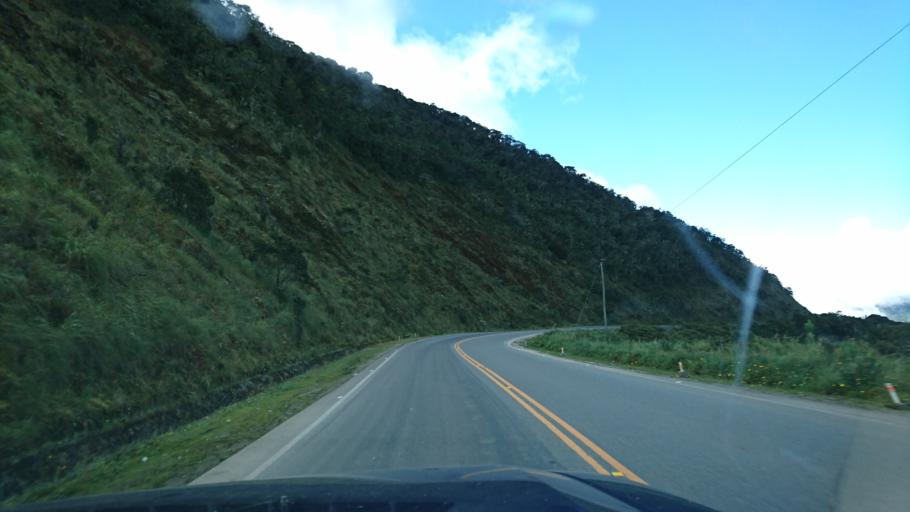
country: BO
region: La Paz
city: Coroico
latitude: -16.2915
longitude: -67.8600
